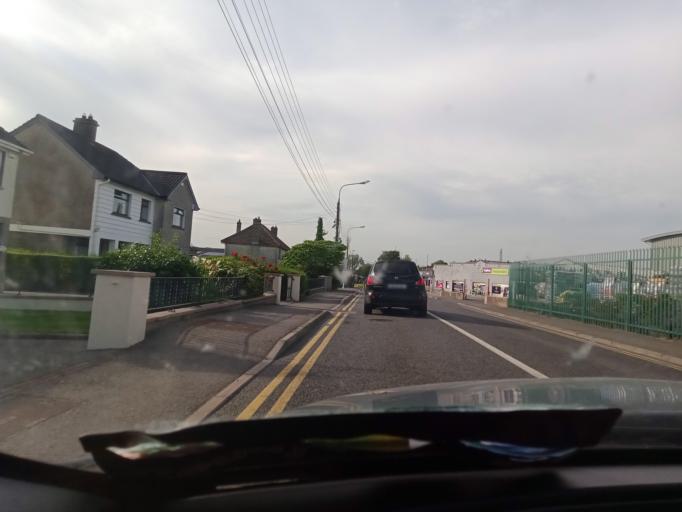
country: IE
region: Ulster
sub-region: An Cabhan
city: Cavan
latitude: 53.9816
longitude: -7.3569
